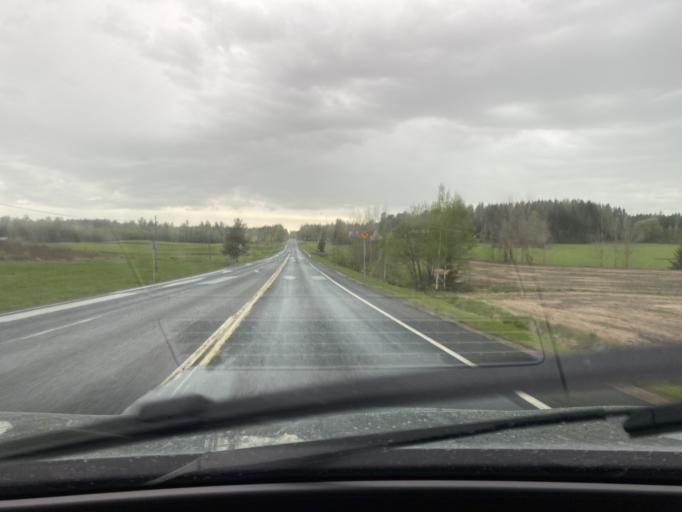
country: FI
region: Varsinais-Suomi
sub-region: Salo
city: Suomusjaervi
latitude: 60.3739
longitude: 23.6237
